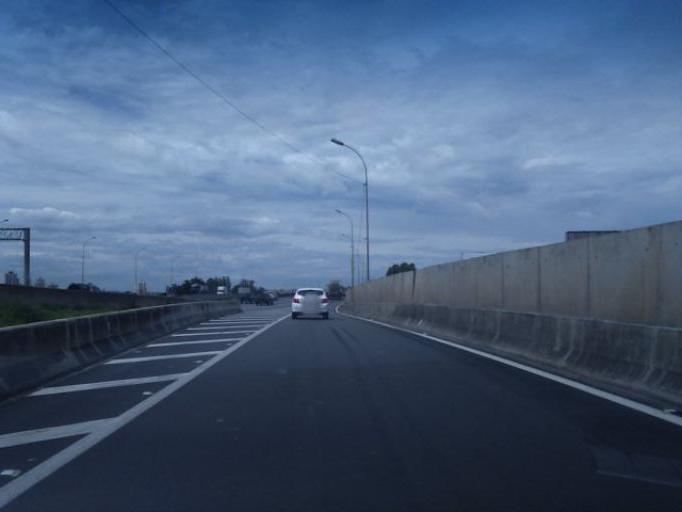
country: BR
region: Sao Paulo
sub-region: Carapicuiba
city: Carapicuiba
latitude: -23.5124
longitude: -46.8100
